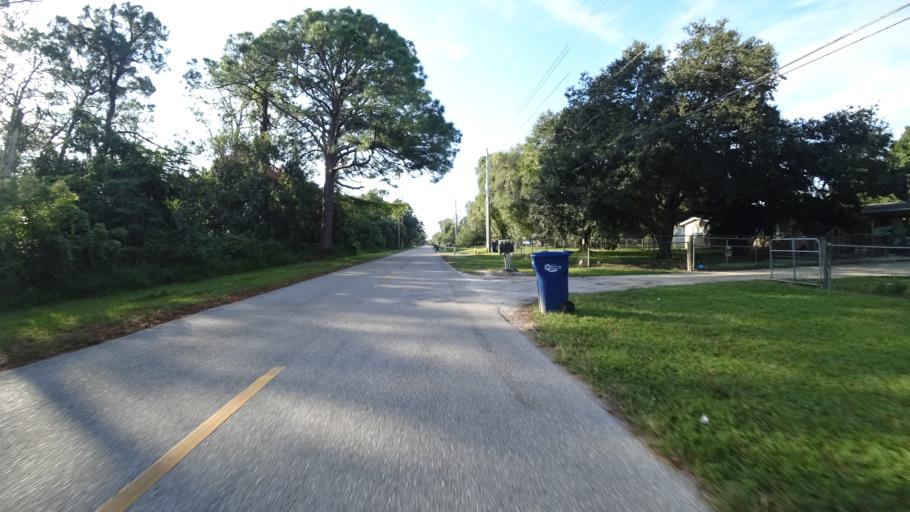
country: US
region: Florida
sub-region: Manatee County
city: Samoset
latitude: 27.4666
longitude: -82.4976
